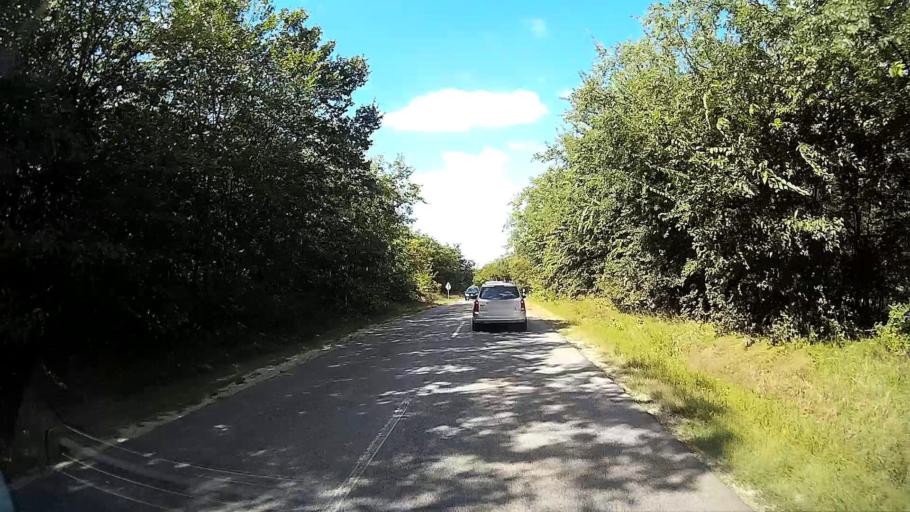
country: HU
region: Pest
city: Mogyorod
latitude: 47.5841
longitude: 19.2319
